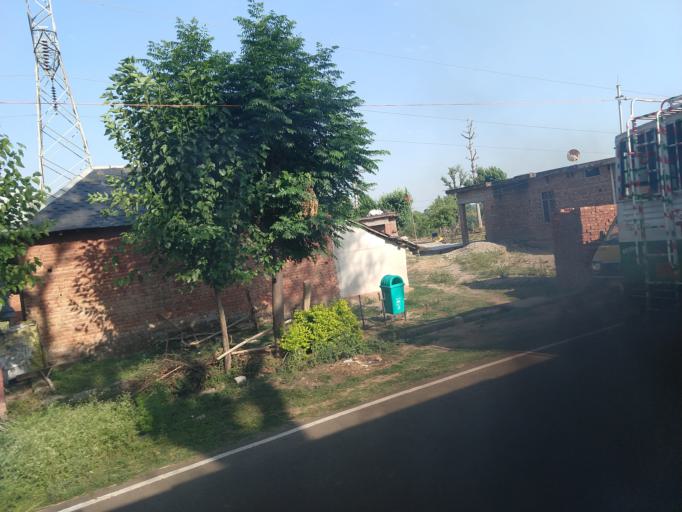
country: IN
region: Himachal Pradesh
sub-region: Chamba
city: Chowari
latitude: 32.3567
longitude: 75.9199
